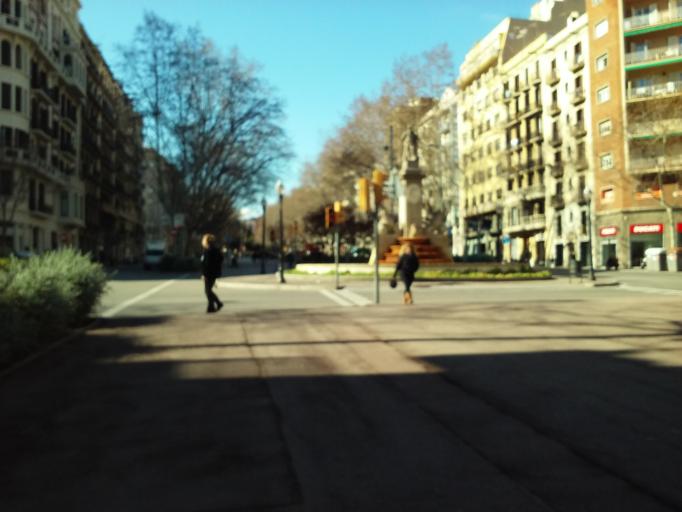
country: ES
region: Catalonia
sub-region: Provincia de Barcelona
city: Gracia
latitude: 41.4016
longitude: 2.1668
